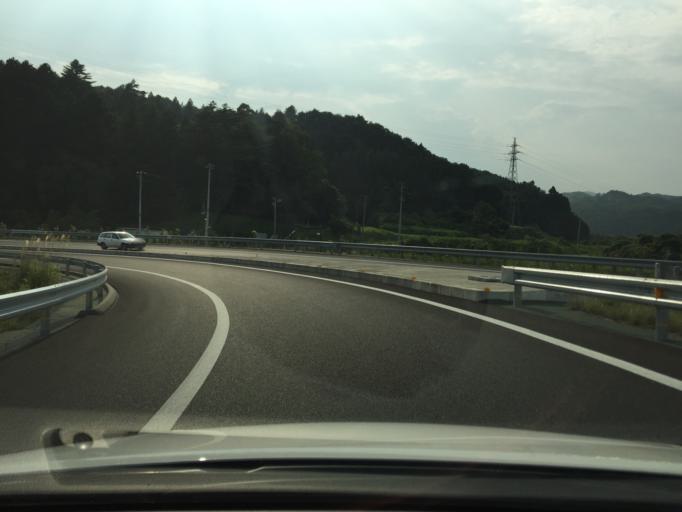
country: JP
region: Fukushima
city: Namie
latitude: 37.6591
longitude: 140.9194
